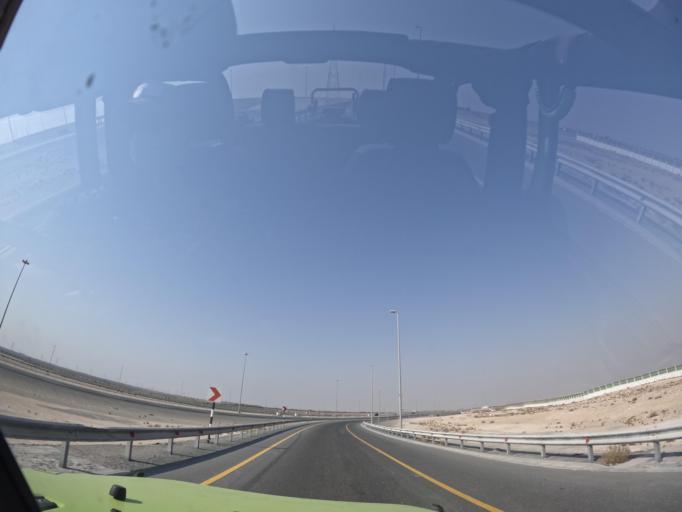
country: AE
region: Abu Dhabi
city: Abu Dhabi
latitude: 24.6167
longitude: 54.7669
